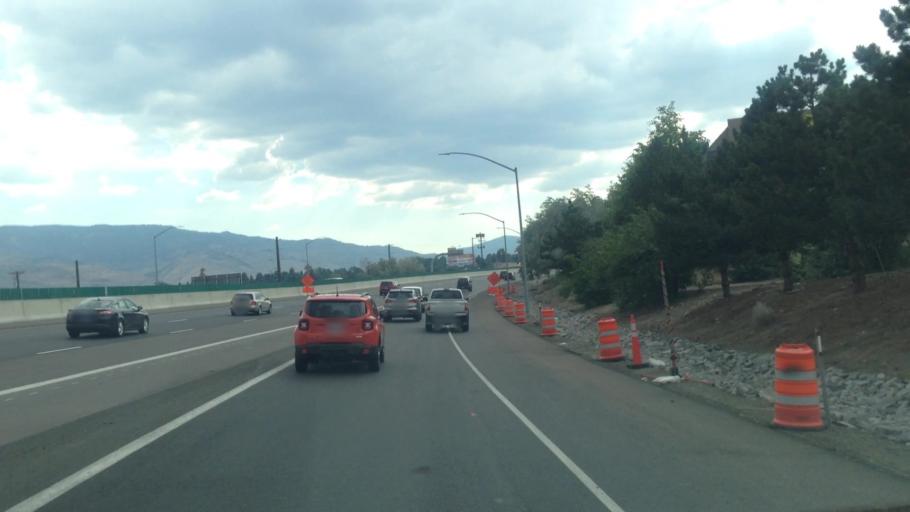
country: US
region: Nevada
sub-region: Washoe County
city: Reno
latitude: 39.5281
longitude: -119.8334
